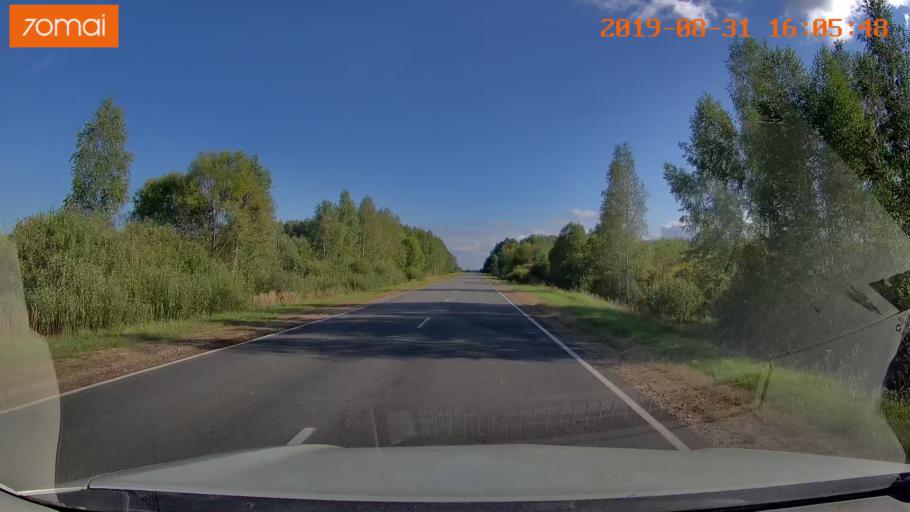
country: RU
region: Kaluga
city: Yukhnov
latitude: 54.6336
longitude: 35.3387
